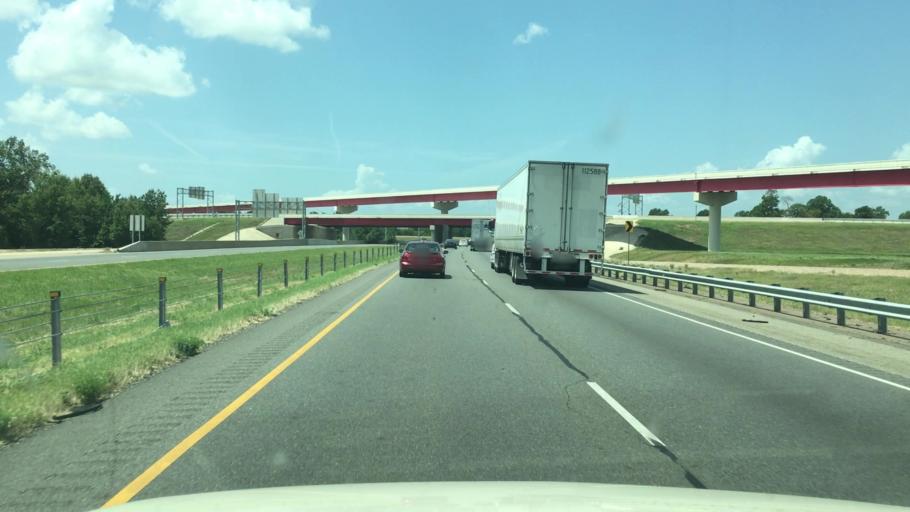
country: US
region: Arkansas
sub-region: Miller County
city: Texarkana
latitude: 33.4809
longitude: -93.9840
